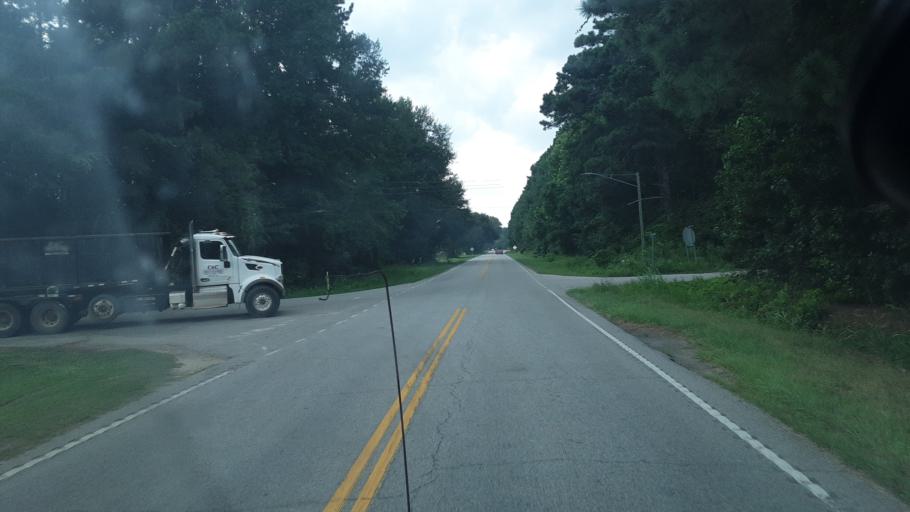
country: US
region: South Carolina
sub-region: Sumter County
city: Sumter
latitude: 33.9687
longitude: -80.3544
